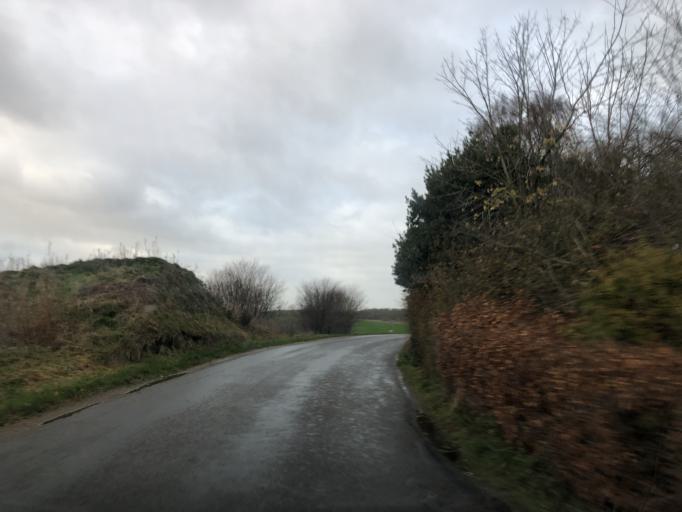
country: DK
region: North Denmark
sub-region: Vesthimmerland Kommune
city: Alestrup
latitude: 56.5935
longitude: 9.6083
